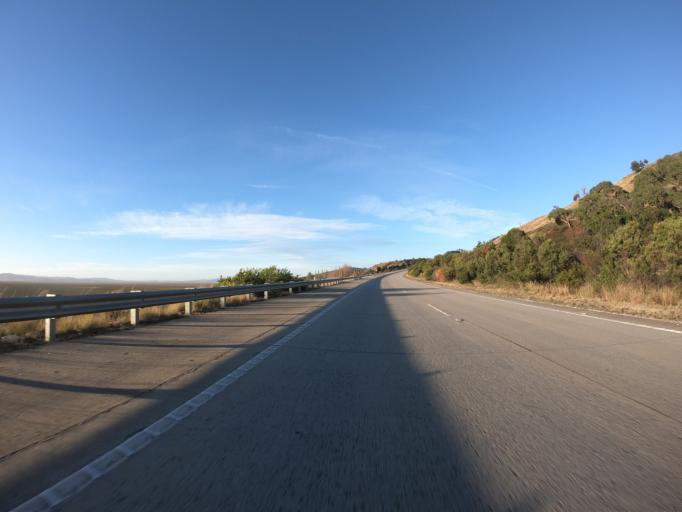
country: AU
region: New South Wales
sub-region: Yass Valley
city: Gundaroo
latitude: -35.0955
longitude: 149.3764
